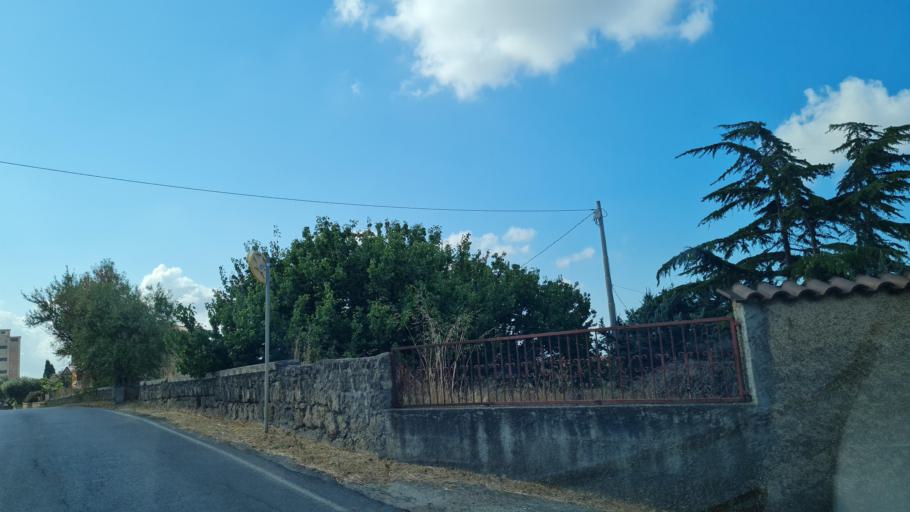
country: IT
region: Latium
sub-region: Provincia di Viterbo
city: Tarquinia
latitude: 42.2512
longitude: 11.7501
